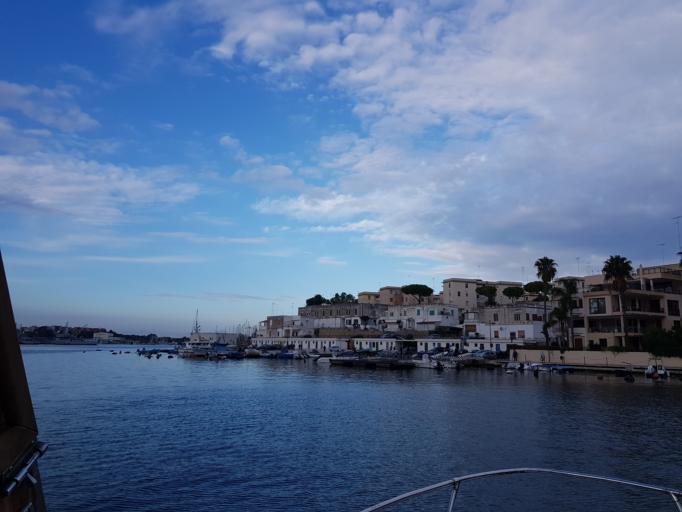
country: IT
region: Apulia
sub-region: Provincia di Brindisi
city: Brindisi
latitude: 40.6431
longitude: 17.9432
